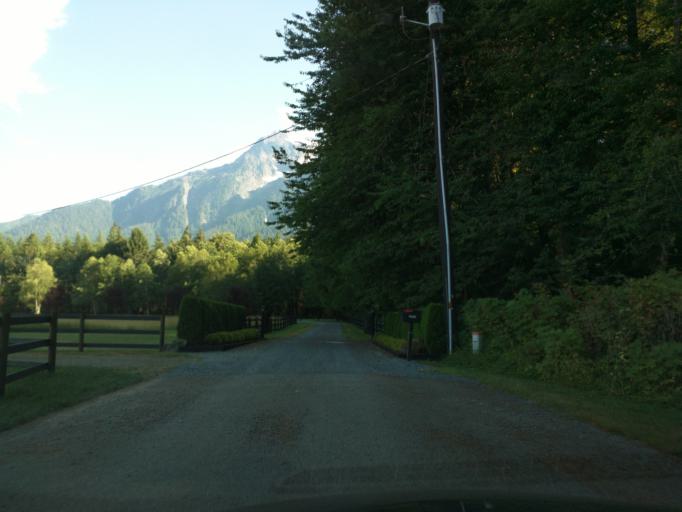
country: US
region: Washington
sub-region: Snohomish County
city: Darrington
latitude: 48.2631
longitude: -121.6815
